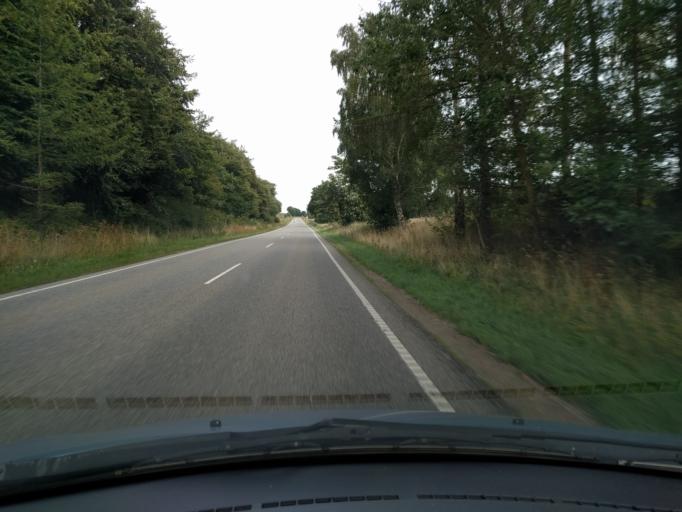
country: DK
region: Zealand
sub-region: Vordingborg Kommune
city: Nyrad
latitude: 55.0154
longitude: 11.9625
